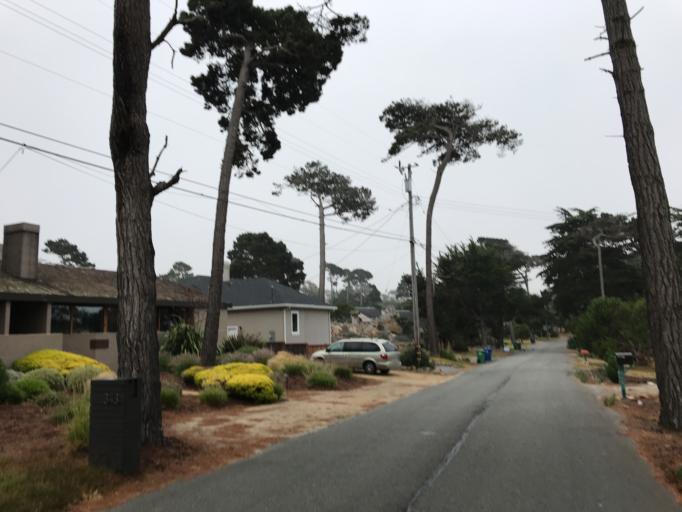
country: US
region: California
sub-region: Monterey County
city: Pacific Grove
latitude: 36.6264
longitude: -121.9352
